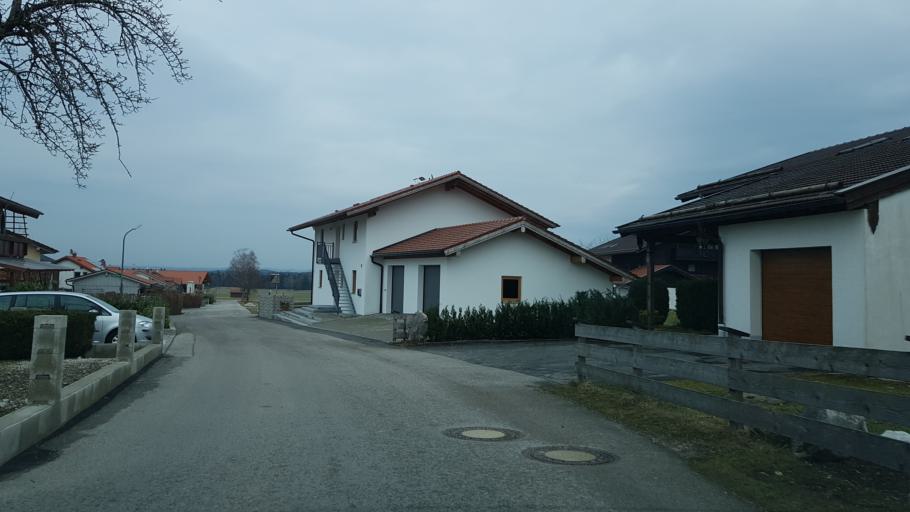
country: DE
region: Bavaria
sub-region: Upper Bavaria
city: Bernau am Chiemsee
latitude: 47.8052
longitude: 12.3759
